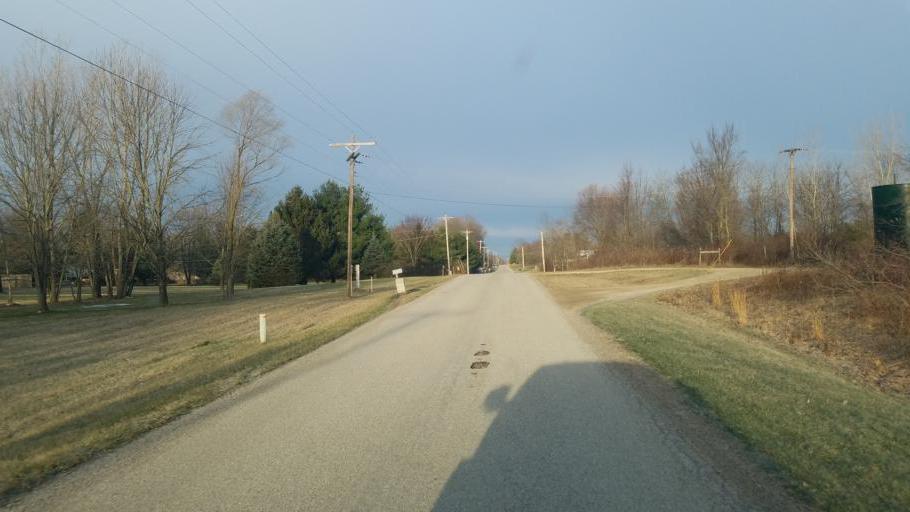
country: US
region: Ohio
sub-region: Knox County
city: Centerburg
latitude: 40.3906
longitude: -82.7483
